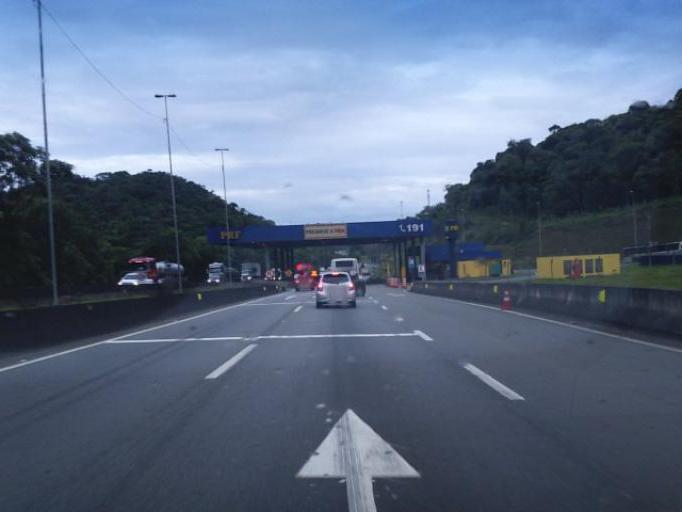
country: BR
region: Parana
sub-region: Sao Jose Dos Pinhais
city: Sao Jose dos Pinhais
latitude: -25.8531
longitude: -48.9784
